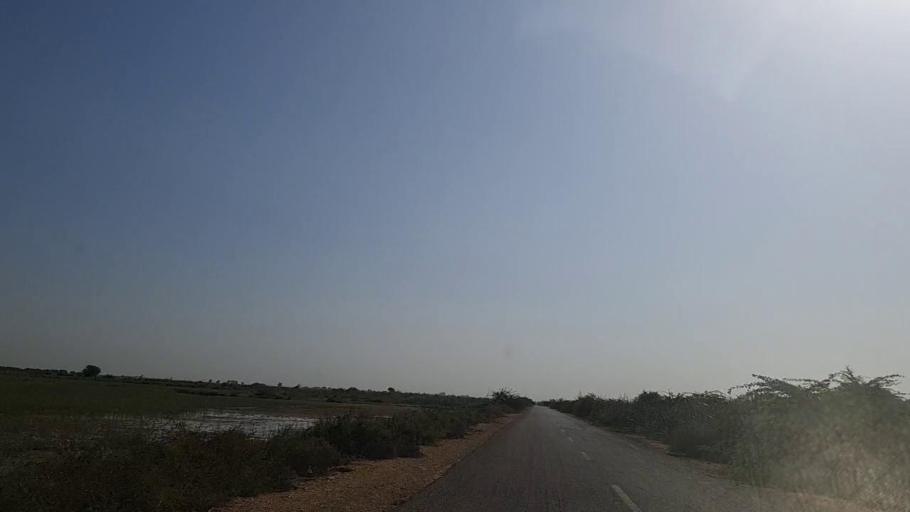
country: PK
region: Sindh
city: Jati
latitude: 24.4470
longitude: 68.2627
